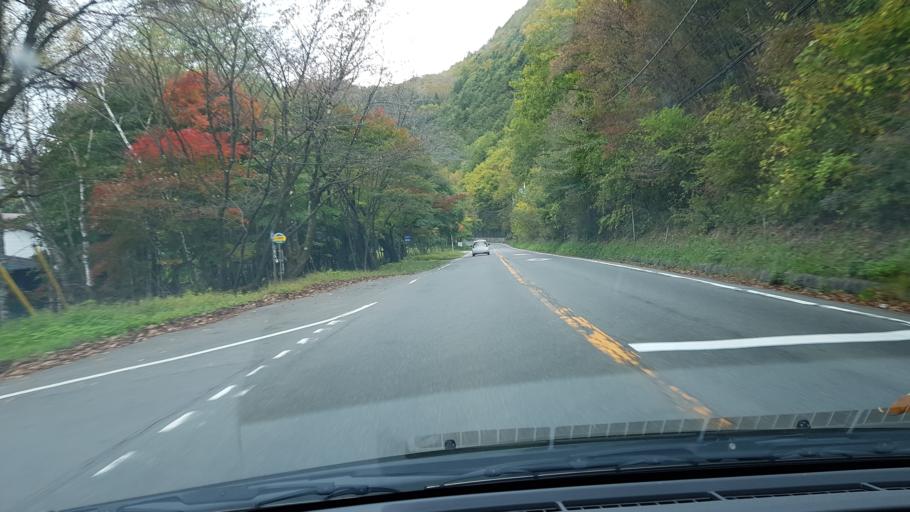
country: JP
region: Gunma
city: Nakanojomachi
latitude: 36.6120
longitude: 138.5870
